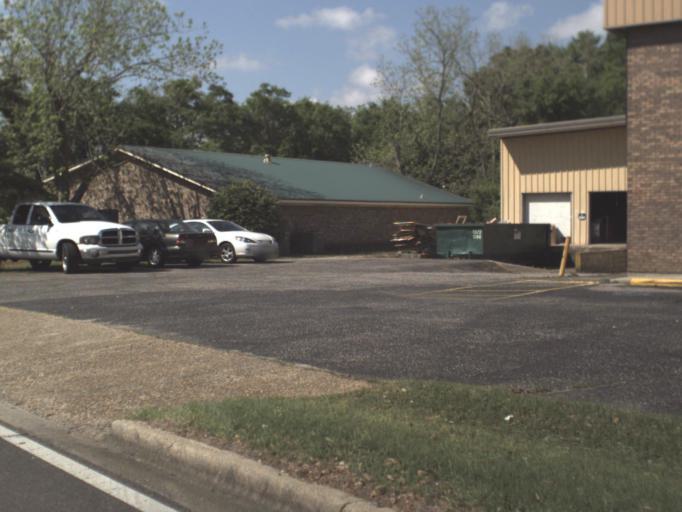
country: US
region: Florida
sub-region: Escambia County
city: Brent
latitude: 30.4650
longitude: -87.2243
